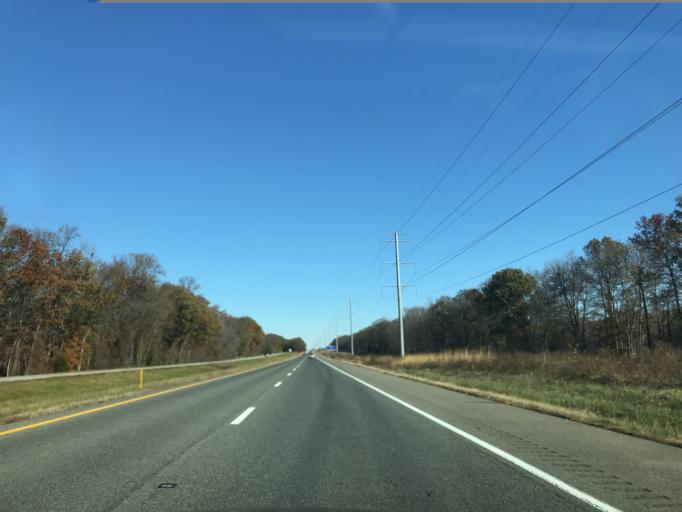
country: US
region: Maryland
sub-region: Queen Anne's County
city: Centreville
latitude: 39.0647
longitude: -75.9910
